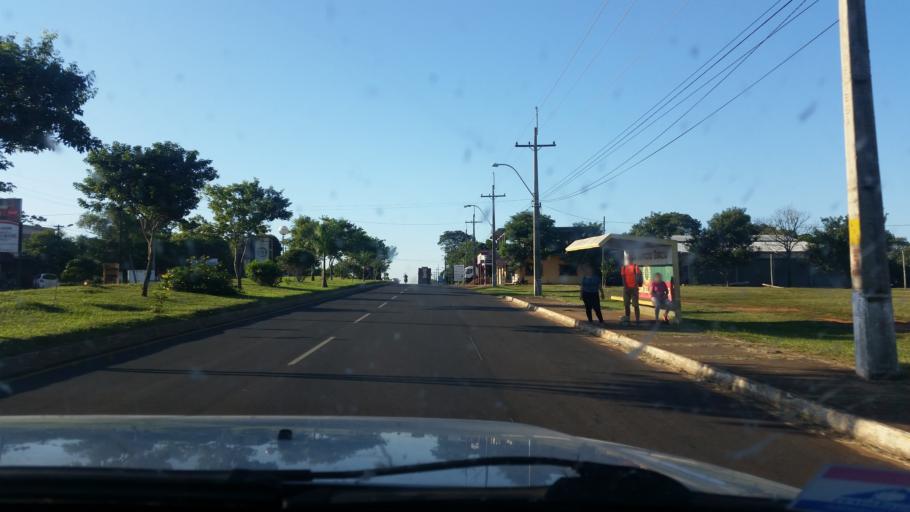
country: PY
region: Misiones
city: Santa Maria
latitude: -26.8811
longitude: -57.0319
